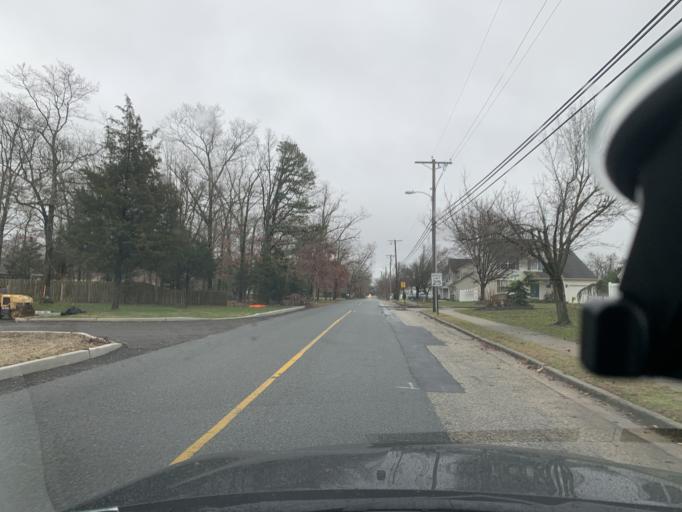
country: US
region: New Jersey
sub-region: Atlantic County
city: Pomona
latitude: 39.4308
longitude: -74.5879
